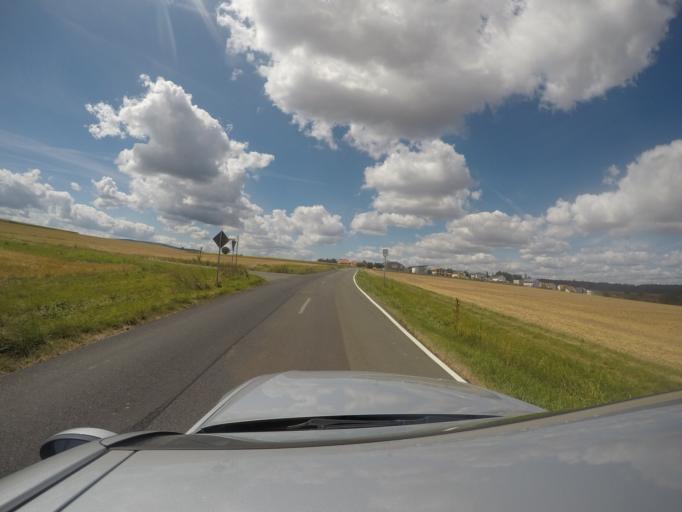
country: DE
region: Rheinland-Pfalz
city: Orbis
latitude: 49.6934
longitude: 8.0028
